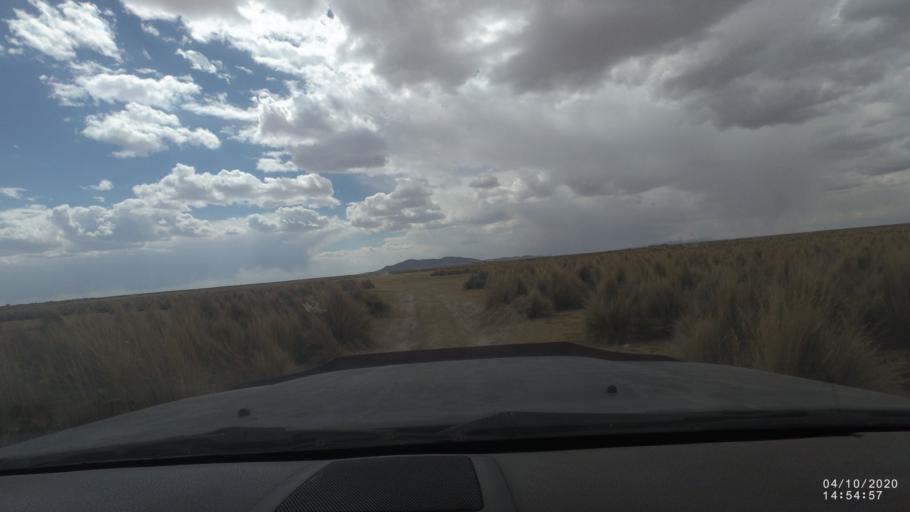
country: BO
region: Oruro
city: Poopo
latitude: -18.6856
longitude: -67.5106
